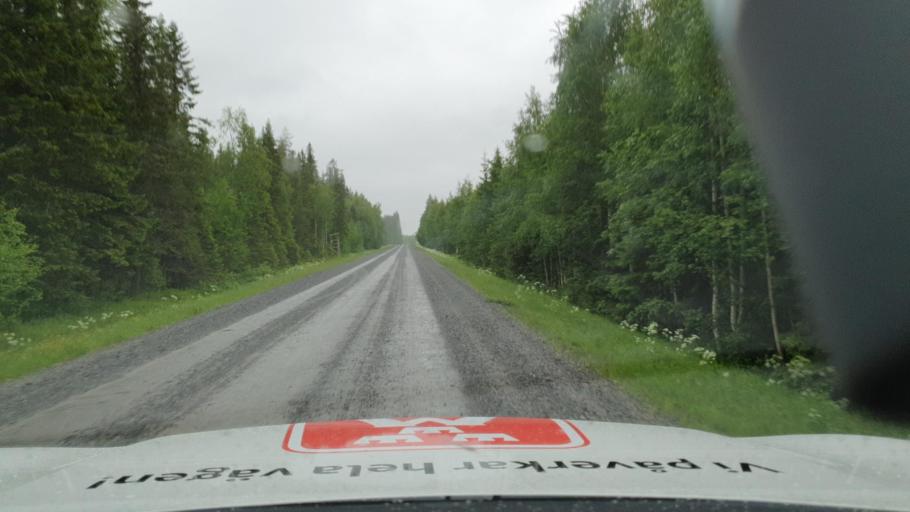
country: SE
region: Vaesterbotten
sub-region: Nordmalings Kommun
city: Nordmaling
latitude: 63.8260
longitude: 19.4907
